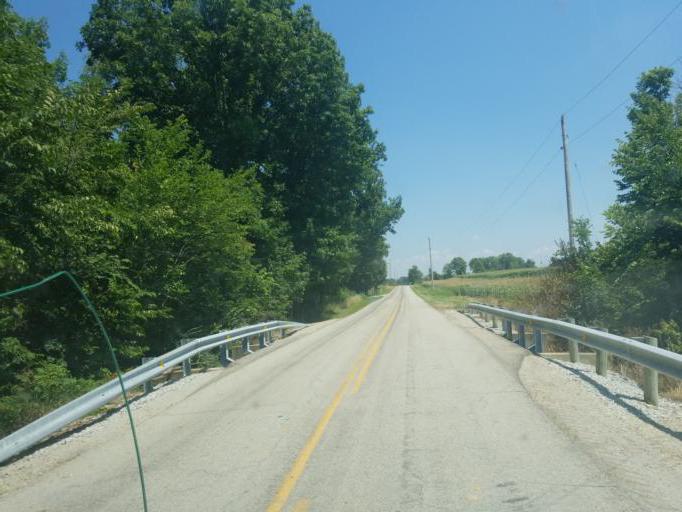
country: US
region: Ohio
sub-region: Shelby County
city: Botkins
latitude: 40.4821
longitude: -84.2260
